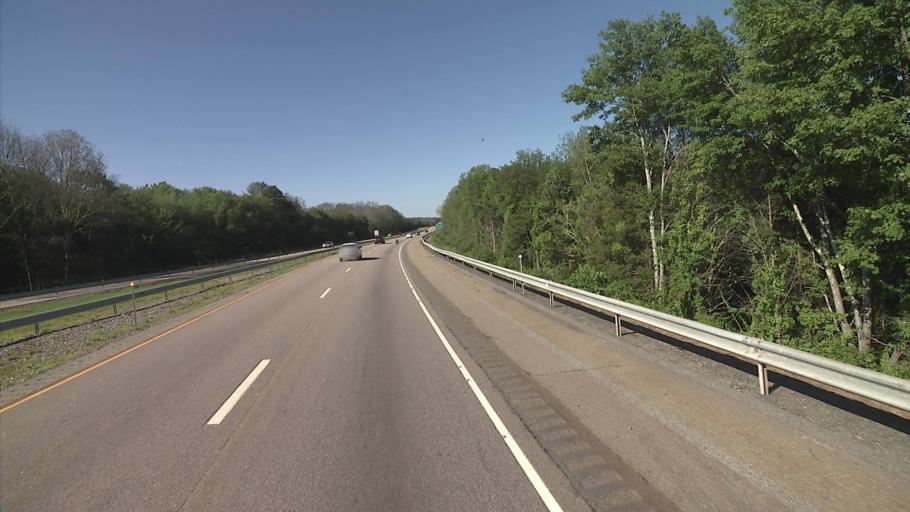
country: US
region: Connecticut
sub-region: New London County
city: Oxoboxo River
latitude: 41.4258
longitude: -72.1267
